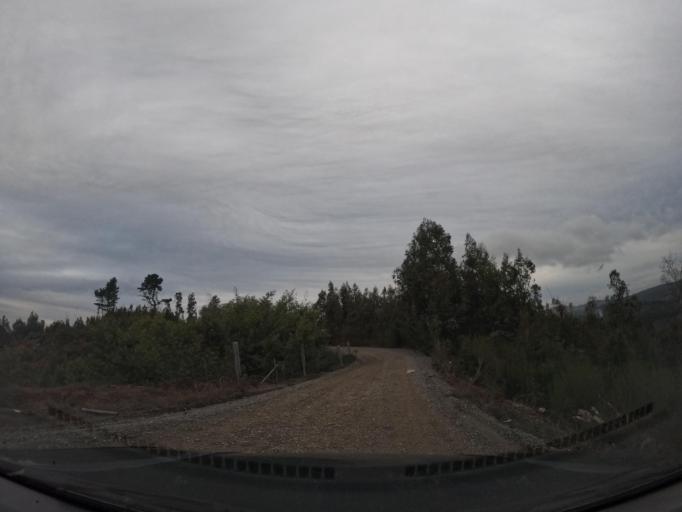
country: CL
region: Biobio
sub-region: Provincia de Concepcion
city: Chiguayante
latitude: -37.0109
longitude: -72.8854
